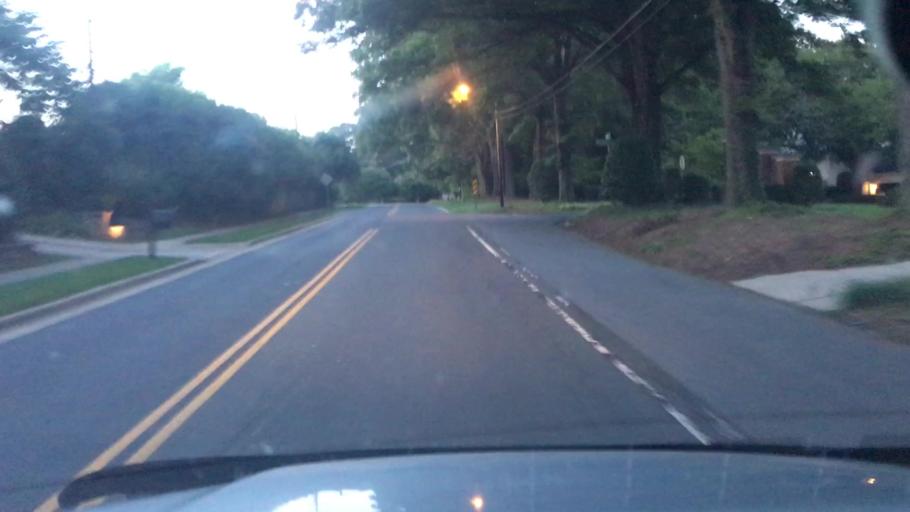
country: US
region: North Carolina
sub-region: Mecklenburg County
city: Matthews
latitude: 35.1354
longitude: -80.8060
